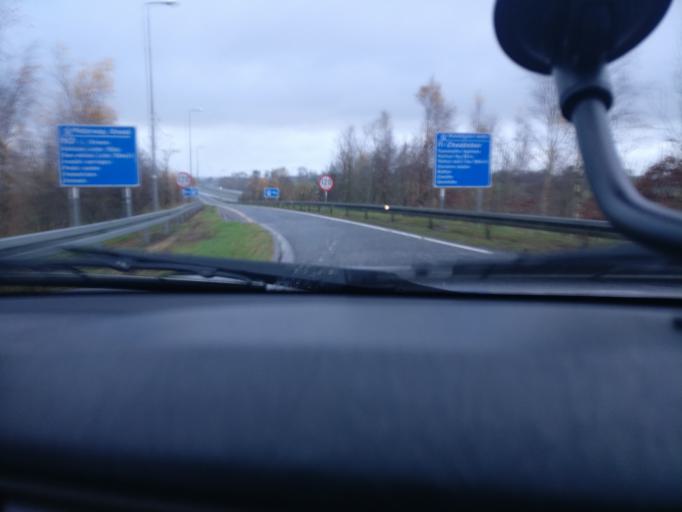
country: IE
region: Leinster
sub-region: An Iarmhi
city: Kinnegad
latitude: 53.4485
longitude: -7.1236
